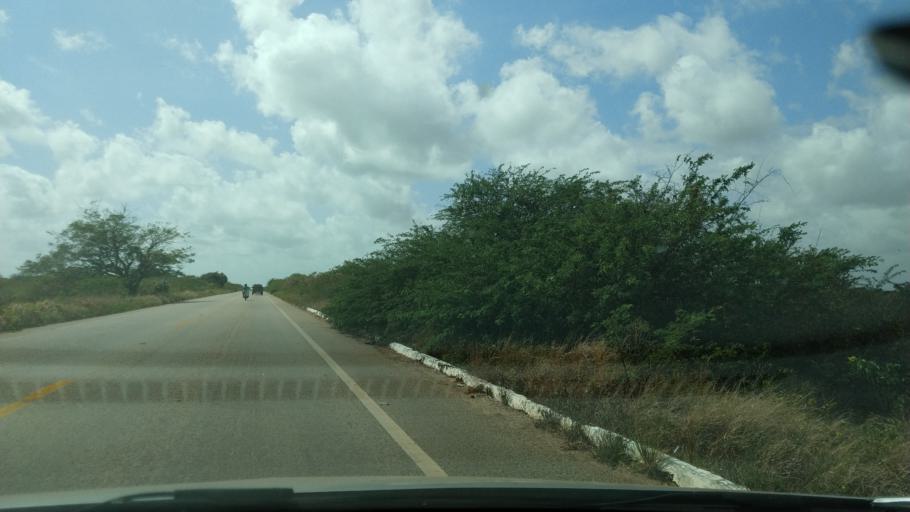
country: BR
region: Rio Grande do Norte
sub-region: Touros
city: Touros
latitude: -5.1895
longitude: -35.5089
